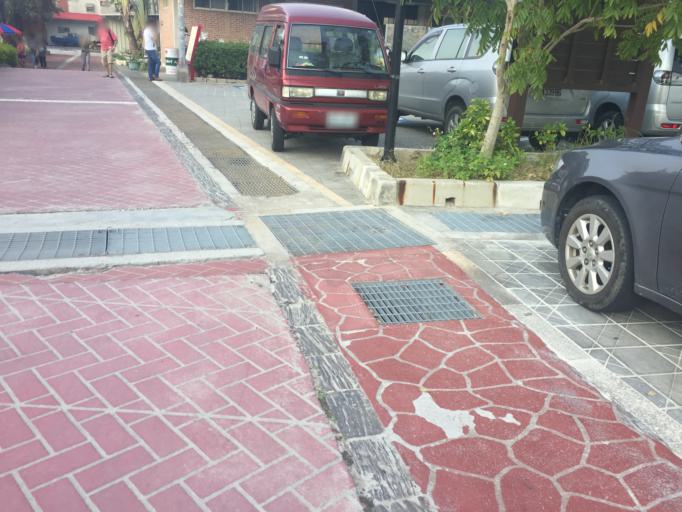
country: TW
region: Taiwan
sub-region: Hsinchu
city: Zhubei
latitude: 24.8769
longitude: 121.0588
